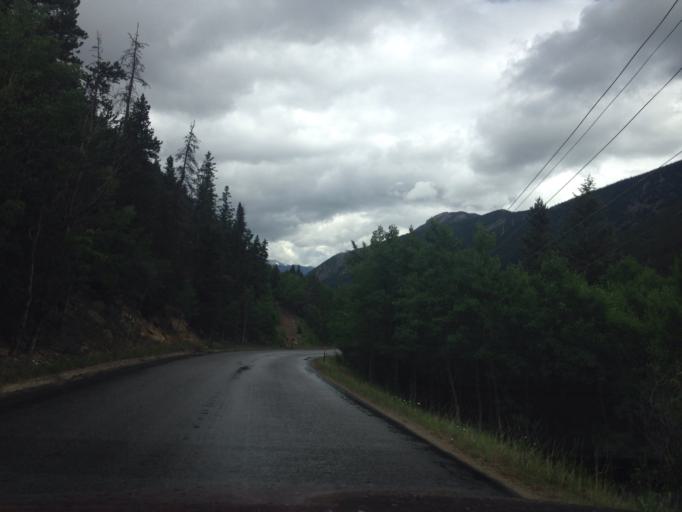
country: US
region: Colorado
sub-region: Clear Creek County
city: Georgetown
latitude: 39.6864
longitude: -105.7009
